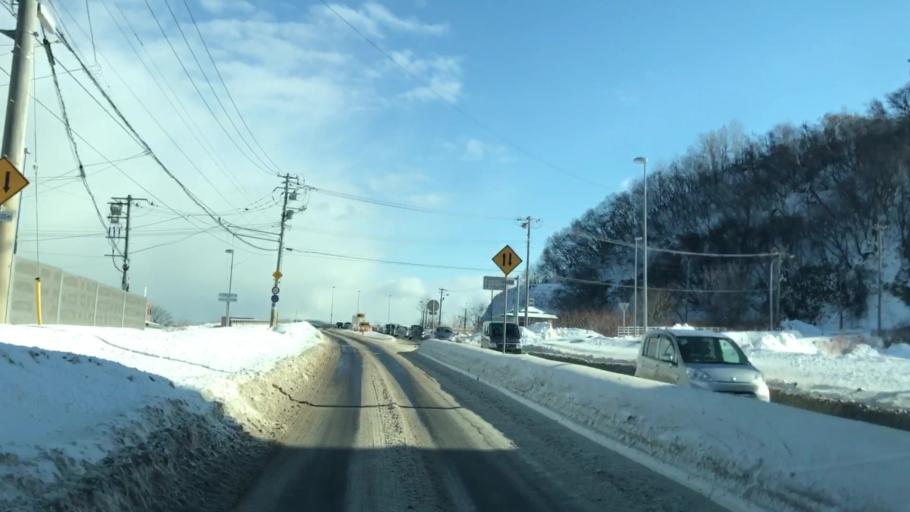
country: JP
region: Hokkaido
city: Otaru
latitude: 43.1821
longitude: 141.0326
